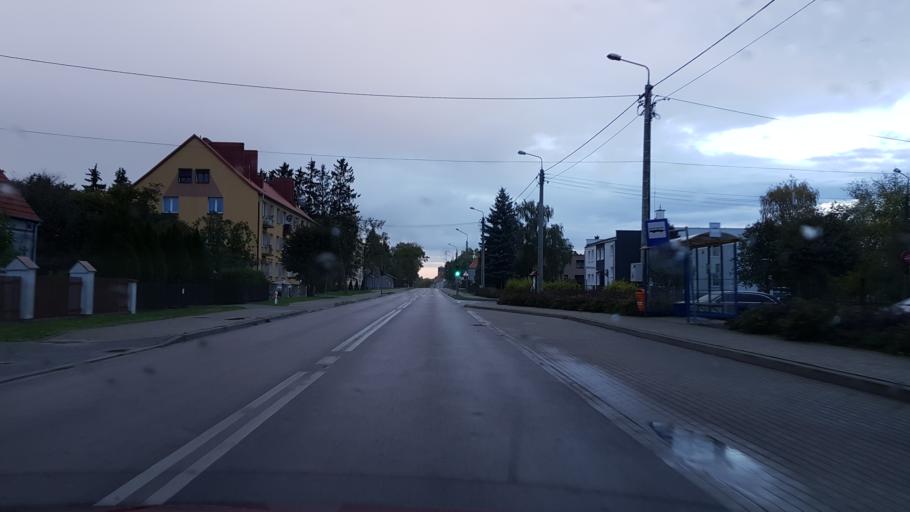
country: PL
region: Greater Poland Voivodeship
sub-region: Powiat zlotowski
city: Krajenka
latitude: 53.2907
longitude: 16.9850
